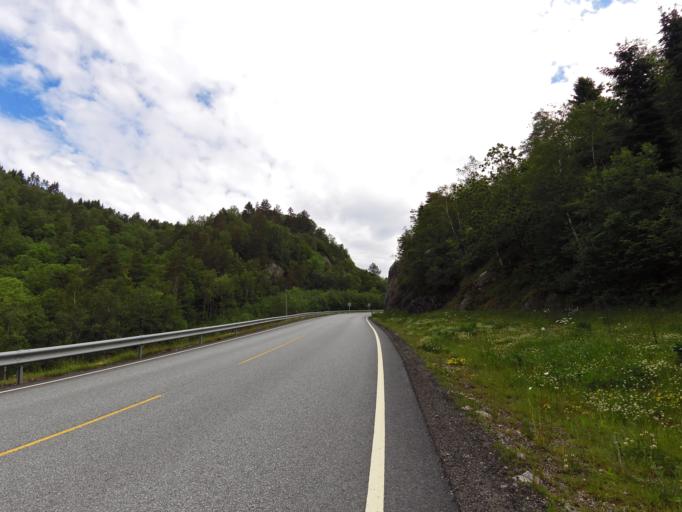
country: NO
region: Vest-Agder
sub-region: Lindesnes
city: Vigeland
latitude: 58.0535
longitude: 7.2105
